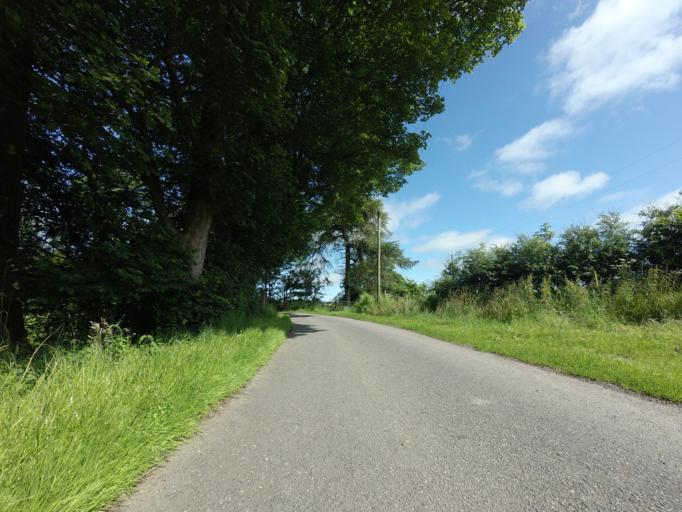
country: GB
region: Scotland
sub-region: Aberdeenshire
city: Turriff
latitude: 57.5856
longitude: -2.5041
